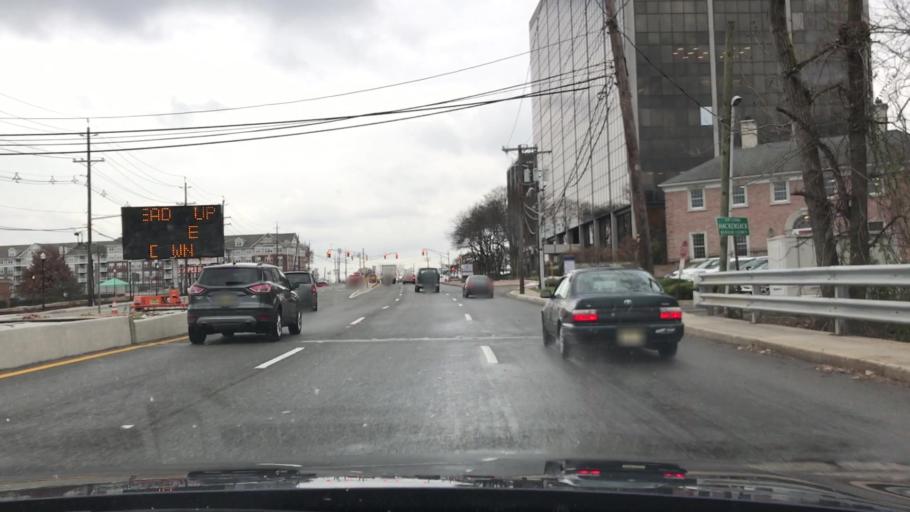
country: US
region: New Jersey
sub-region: Bergen County
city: River Edge
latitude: 40.9112
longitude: -74.0334
